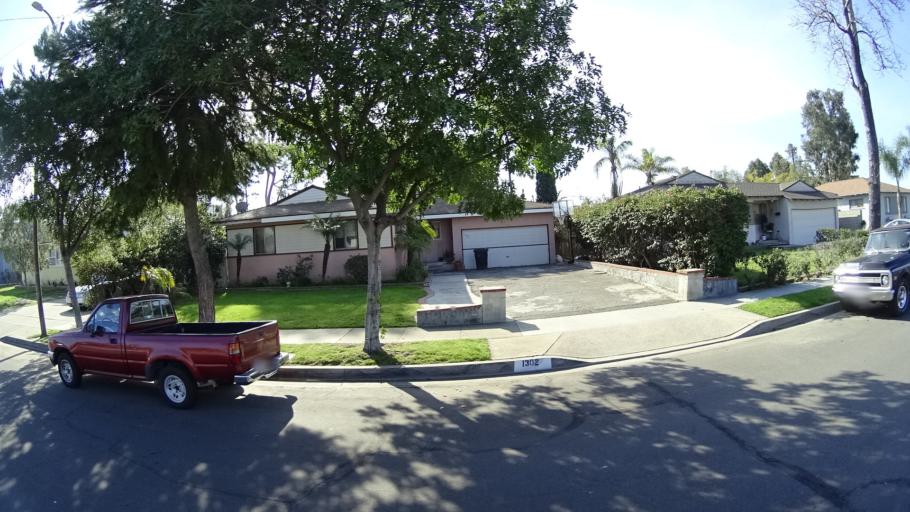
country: US
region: California
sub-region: Orange County
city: Fullerton
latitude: 33.8487
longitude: -117.9364
